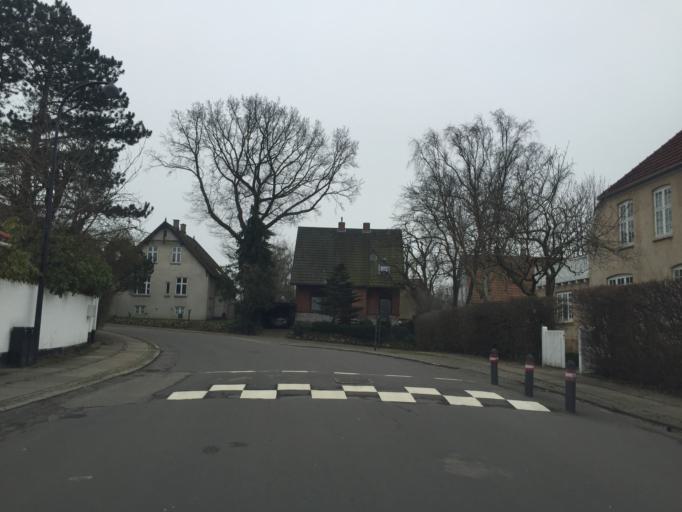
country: DK
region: Capital Region
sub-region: Lyngby-Tarbaek Kommune
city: Kongens Lyngby
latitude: 55.7524
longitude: 12.5359
